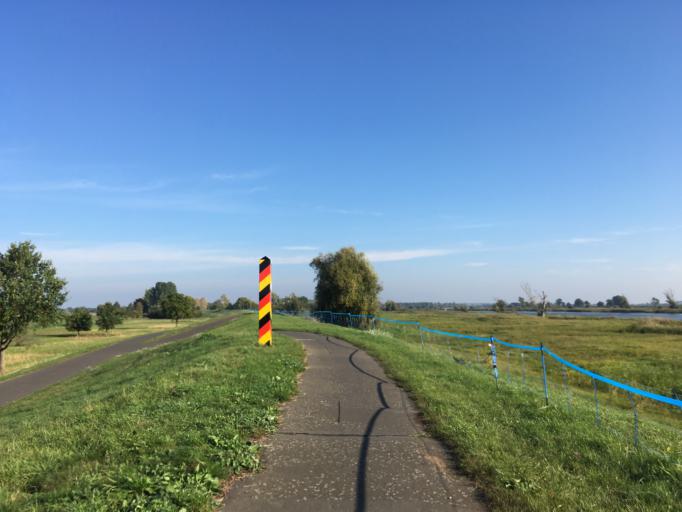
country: DE
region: Brandenburg
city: Reitwein
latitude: 52.5411
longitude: 14.6080
